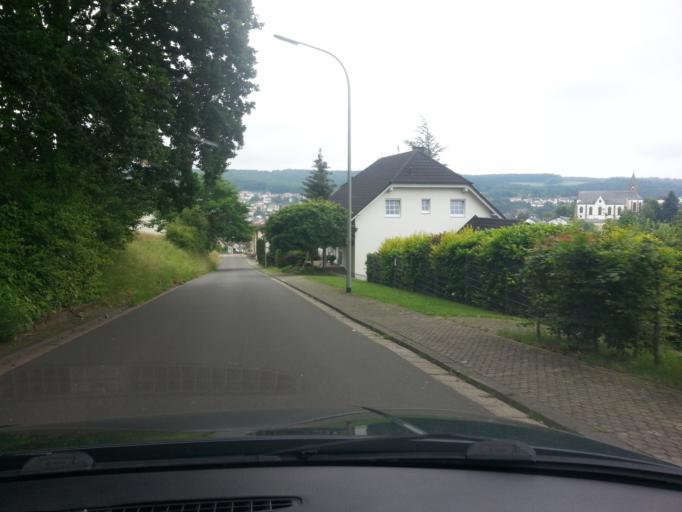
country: DE
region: Saarland
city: Marpingen
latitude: 49.4568
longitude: 7.0506
